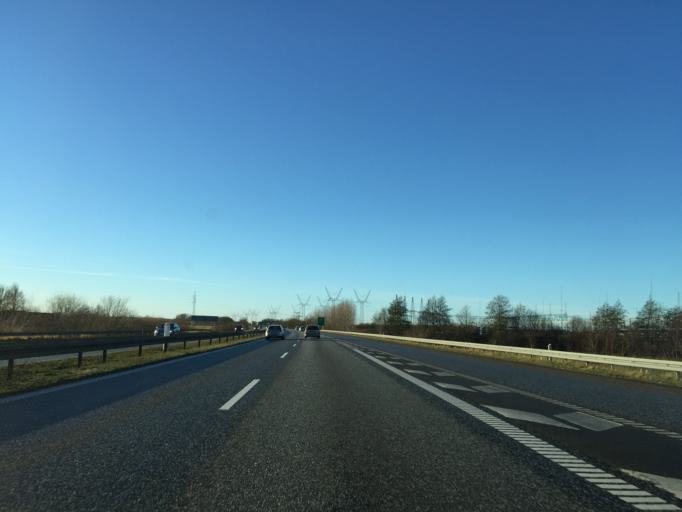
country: DK
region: South Denmark
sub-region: Odense Kommune
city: Neder Holluf
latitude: 55.3650
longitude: 10.5123
